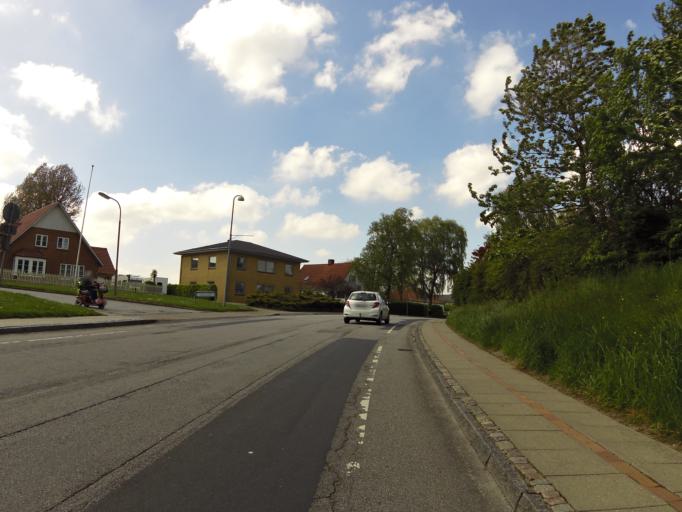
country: DK
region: South Denmark
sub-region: Tonder Kommune
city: Toftlund
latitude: 55.1862
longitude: 9.0665
